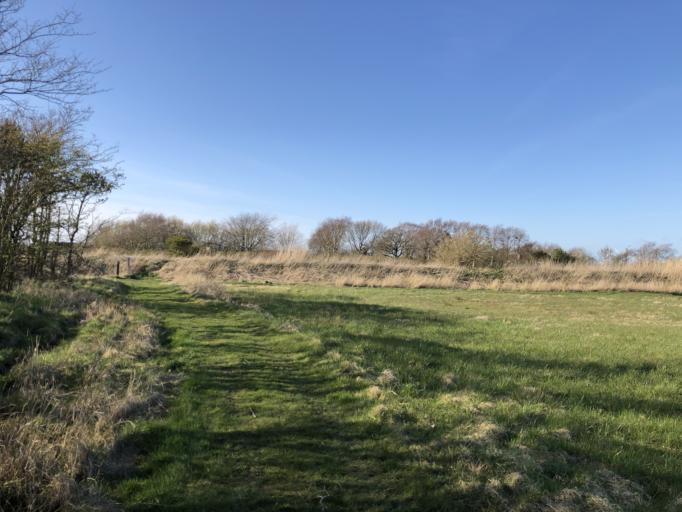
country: DK
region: Central Jutland
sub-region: Holstebro Kommune
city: Ulfborg
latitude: 56.3304
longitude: 8.3133
